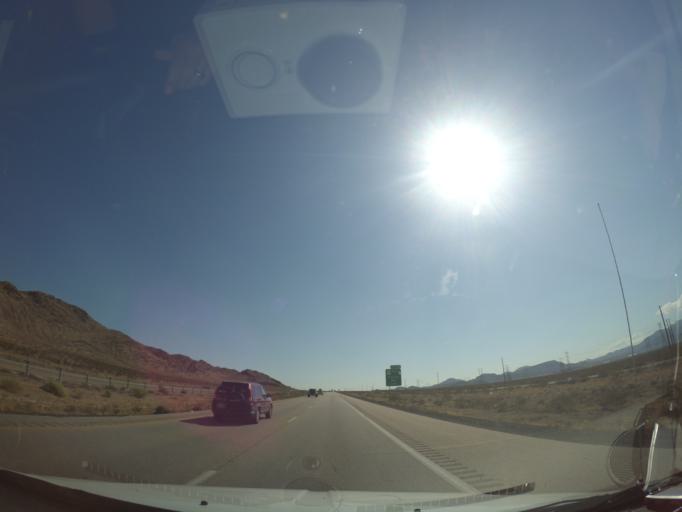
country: US
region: Nevada
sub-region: Clark County
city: Nellis Air Force Base
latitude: 36.3977
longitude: -114.8815
